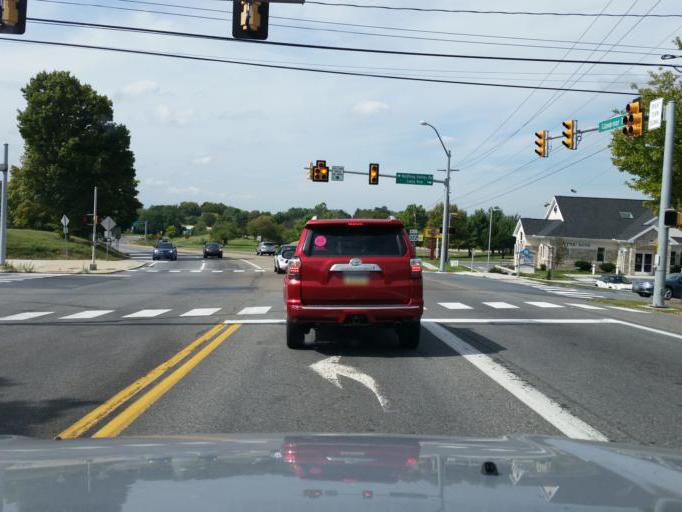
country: US
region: Pennsylvania
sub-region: Dauphin County
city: Hummelstown
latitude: 40.2676
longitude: -76.6816
